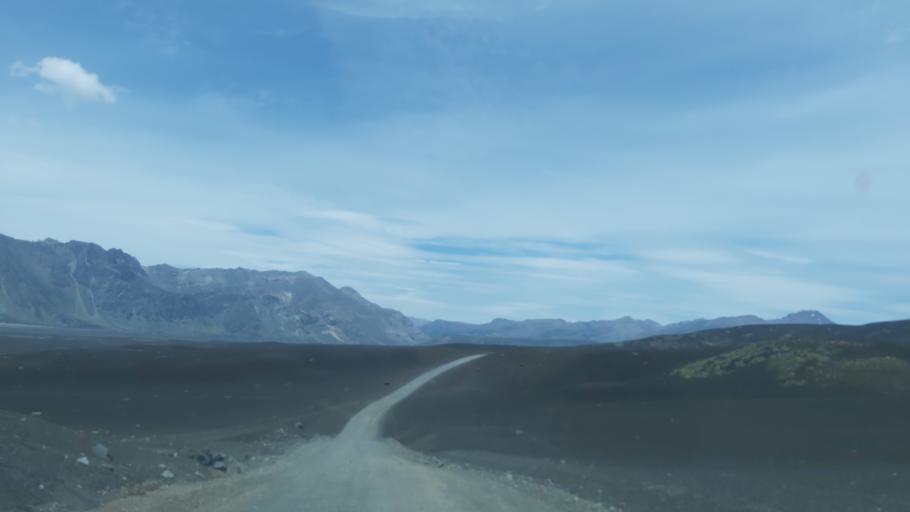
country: AR
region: Neuquen
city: Andacollo
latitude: -37.4161
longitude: -71.2898
